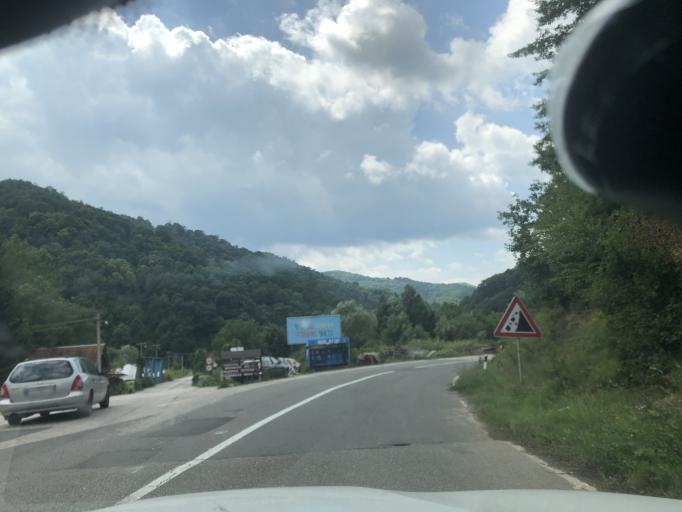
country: RS
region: Central Serbia
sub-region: Jablanicki Okrug
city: Medvega
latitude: 42.8030
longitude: 21.5770
